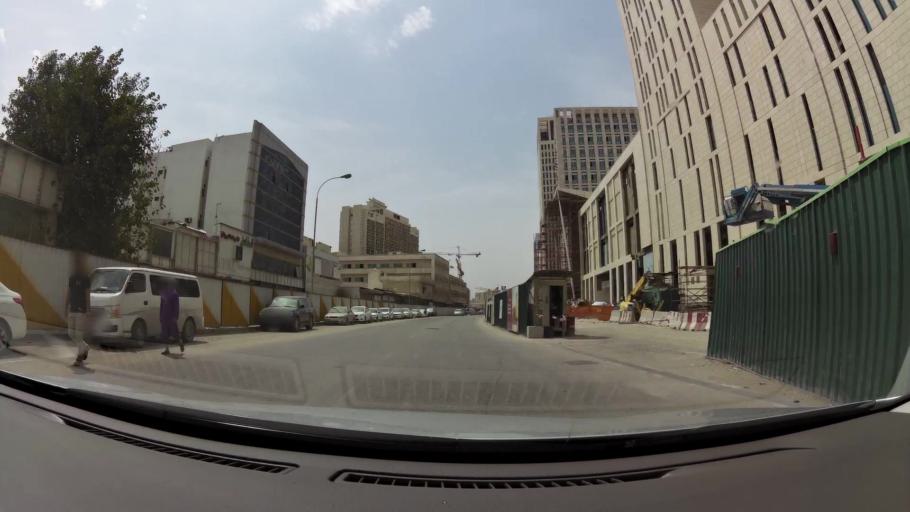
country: QA
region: Baladiyat ad Dawhah
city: Doha
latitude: 25.2846
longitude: 51.5299
